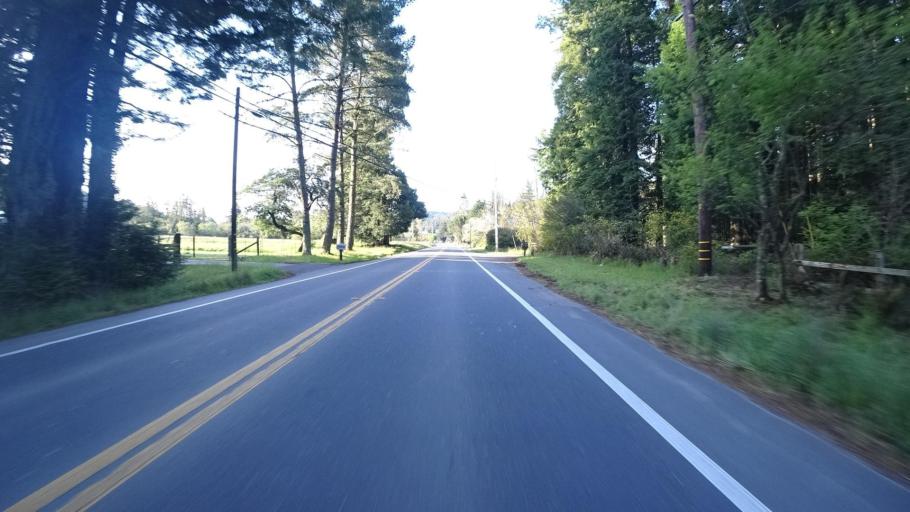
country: US
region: California
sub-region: Humboldt County
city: Myrtletown
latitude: 40.7746
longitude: -124.0736
